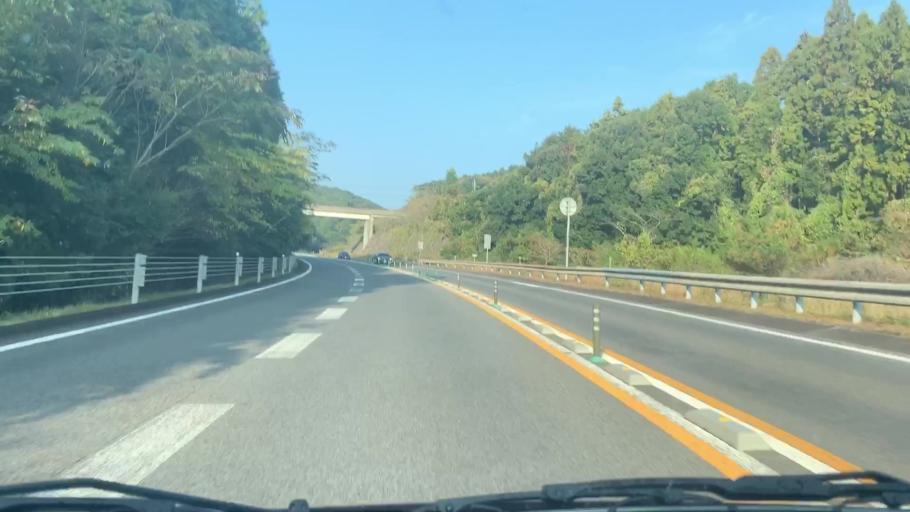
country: JP
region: Saga Prefecture
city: Imaricho-ko
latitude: 33.1588
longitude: 129.8707
